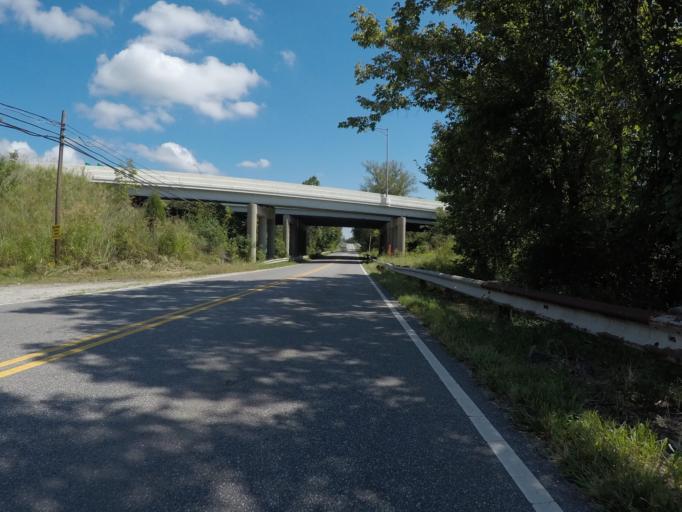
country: US
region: West Virginia
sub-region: Cabell County
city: Huntington
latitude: 38.4217
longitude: -82.4900
